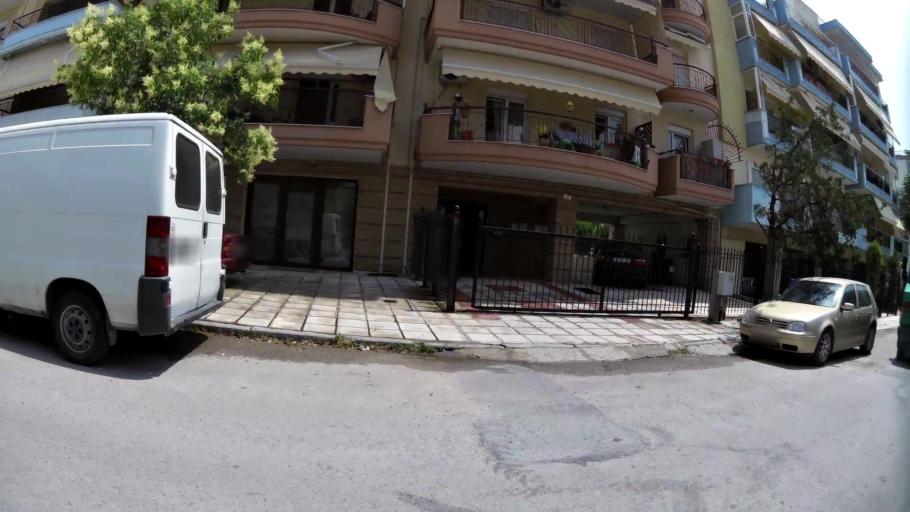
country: GR
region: Central Macedonia
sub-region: Nomos Thessalonikis
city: Evosmos
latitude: 40.6631
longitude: 22.9047
